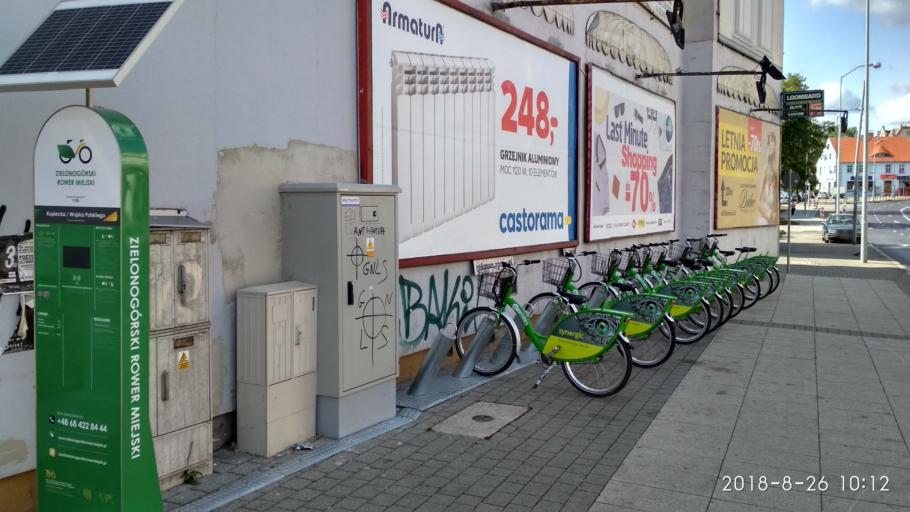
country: PL
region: Lubusz
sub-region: Zielona Gora
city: Zielona Gora
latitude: 51.9413
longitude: 15.5041
